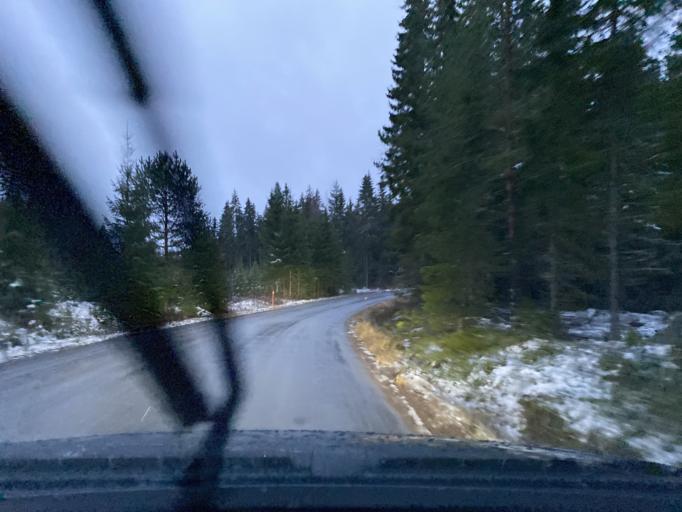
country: FI
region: Pirkanmaa
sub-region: Lounais-Pirkanmaa
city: Punkalaidun
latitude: 61.1483
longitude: 22.9672
